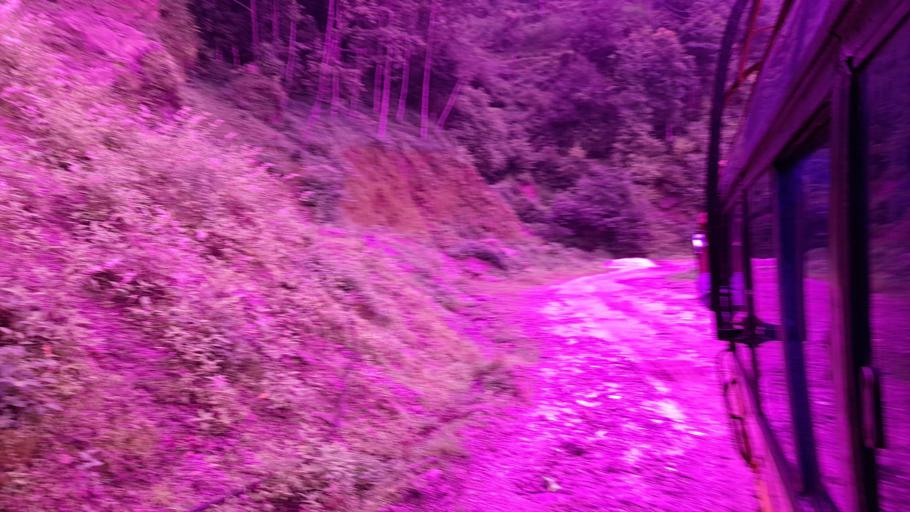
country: NP
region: Central Region
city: Kirtipur
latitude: 27.8123
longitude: 85.2147
